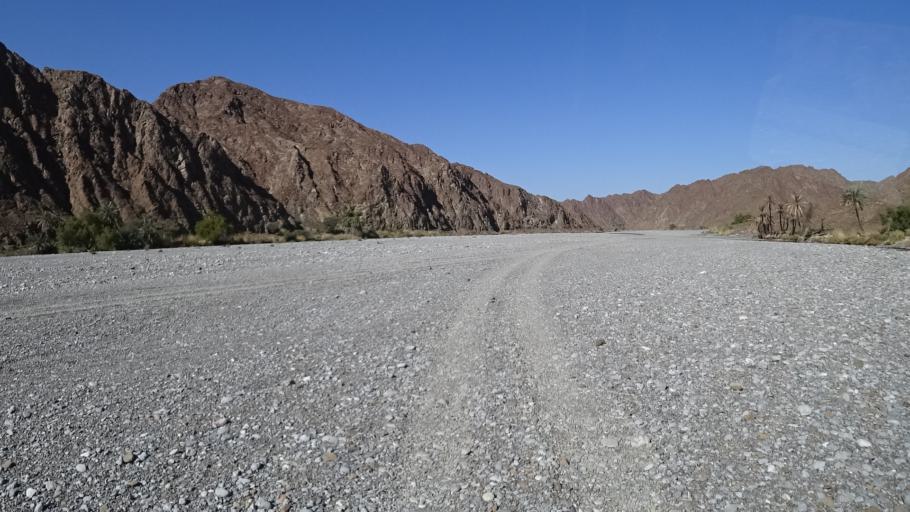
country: OM
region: Al Batinah
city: Bayt al `Awabi
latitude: 23.4055
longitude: 57.6661
